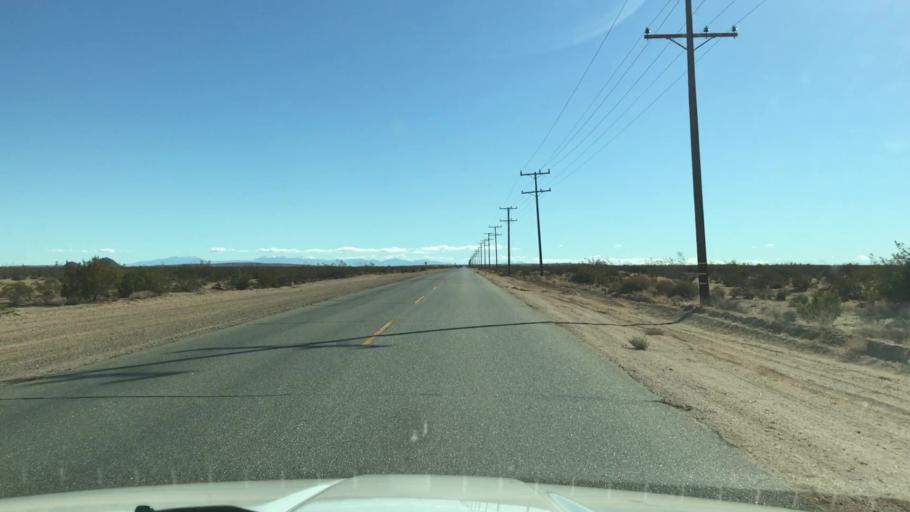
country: US
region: California
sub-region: Kern County
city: California City
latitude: 35.1803
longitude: -117.9858
